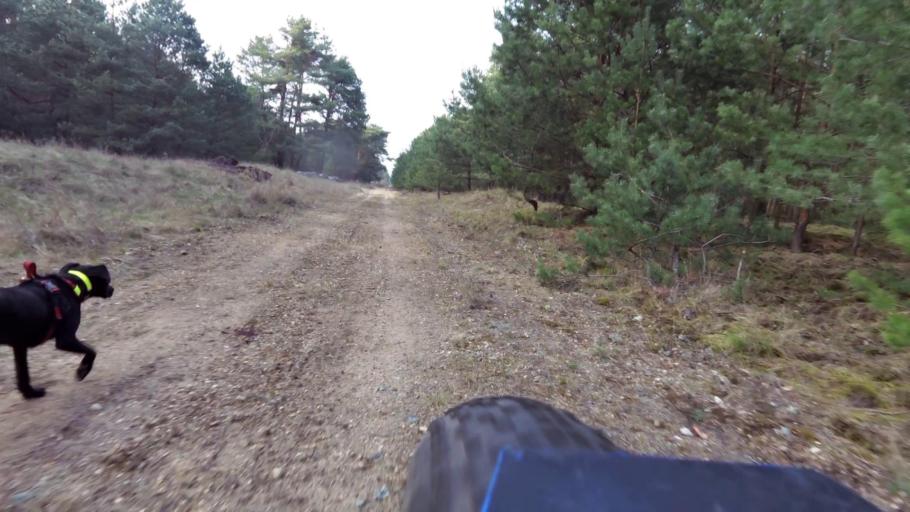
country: DE
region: Brandenburg
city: Vogelsang
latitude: 52.2648
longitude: 14.6919
